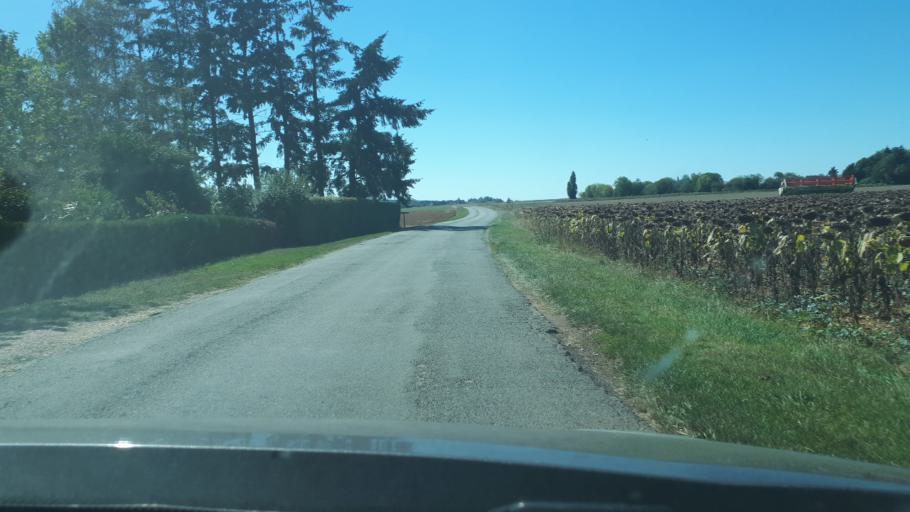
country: FR
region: Centre
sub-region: Departement du Cher
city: Rians
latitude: 47.1988
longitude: 2.7228
